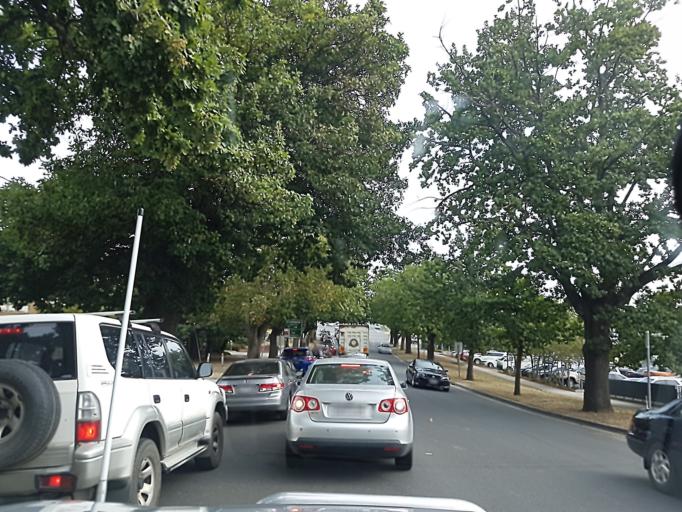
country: AU
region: Victoria
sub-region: Yarra Ranges
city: Lilydale
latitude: -37.7563
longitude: 145.3551
